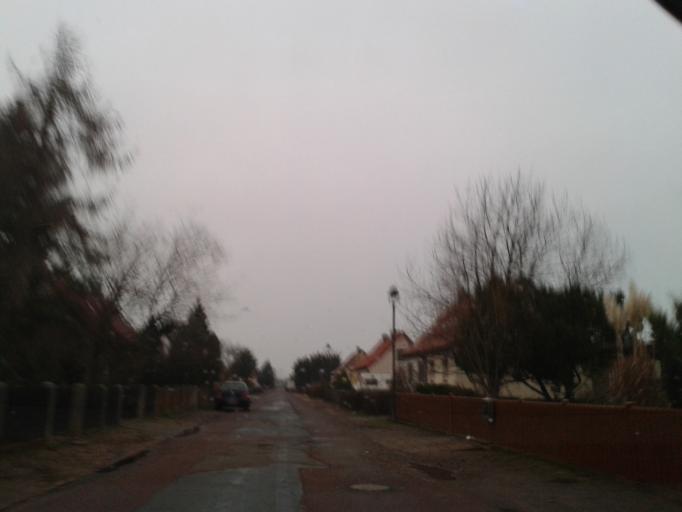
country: DE
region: Saxony-Anhalt
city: Peissen
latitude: 51.4906
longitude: 12.0295
